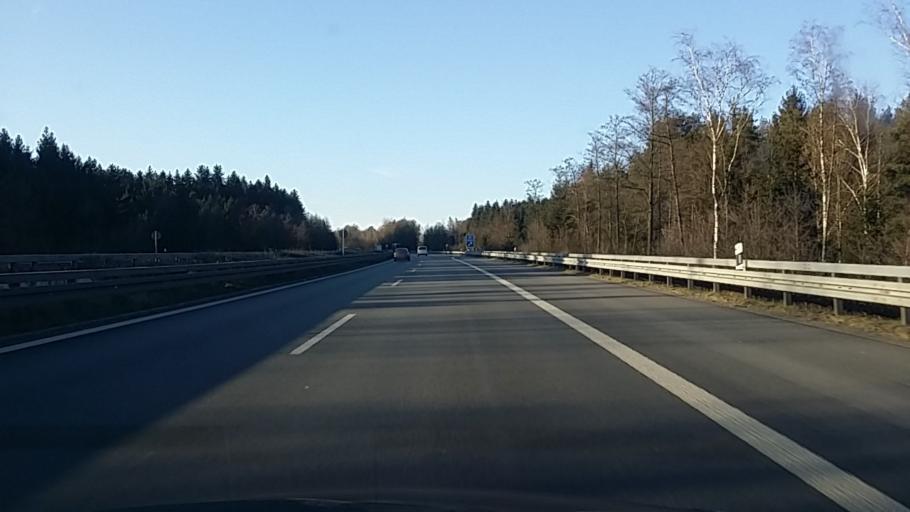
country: DE
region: Bavaria
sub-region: Lower Bavaria
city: Haselbach
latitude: 48.6171
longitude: 13.3553
